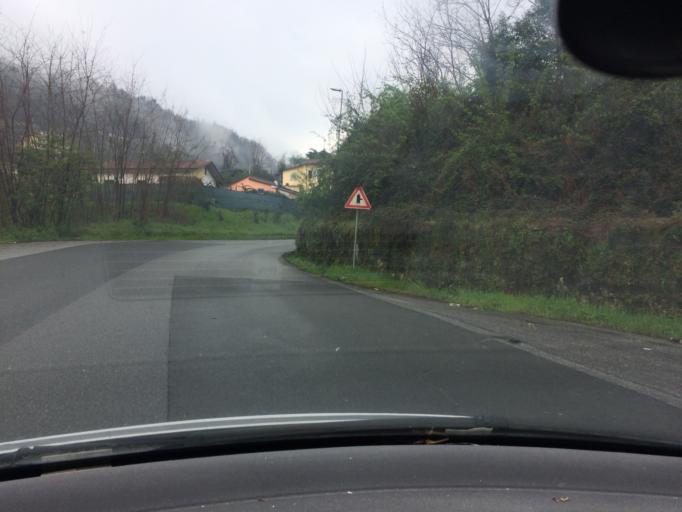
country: IT
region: Tuscany
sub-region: Provincia di Massa-Carrara
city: Carrara
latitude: 44.0710
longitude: 10.1060
